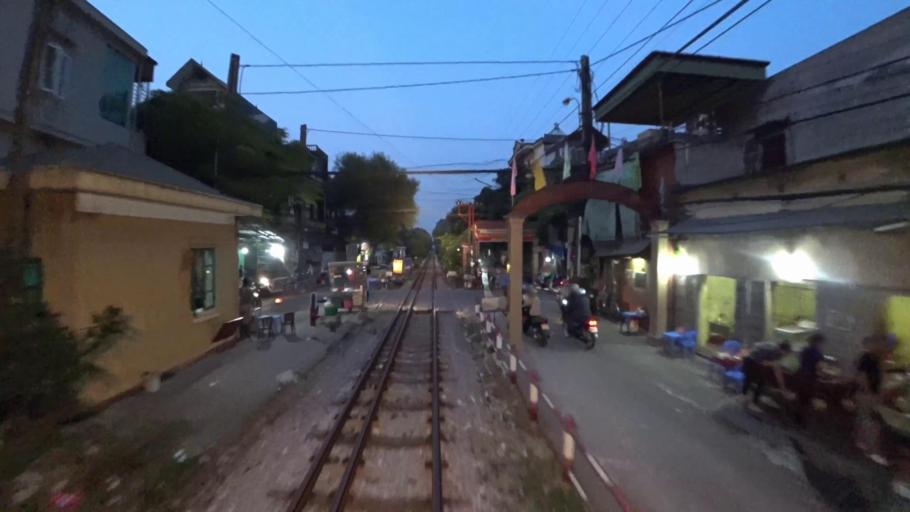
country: VN
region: Ha Noi
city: Soc Son
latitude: 21.2533
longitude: 105.8618
